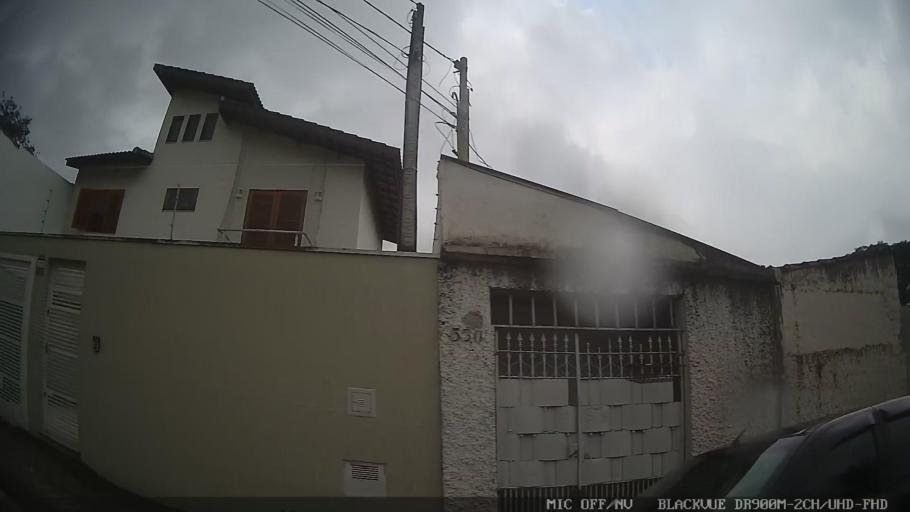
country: BR
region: Sao Paulo
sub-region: Mogi das Cruzes
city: Mogi das Cruzes
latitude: -23.5238
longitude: -46.1788
